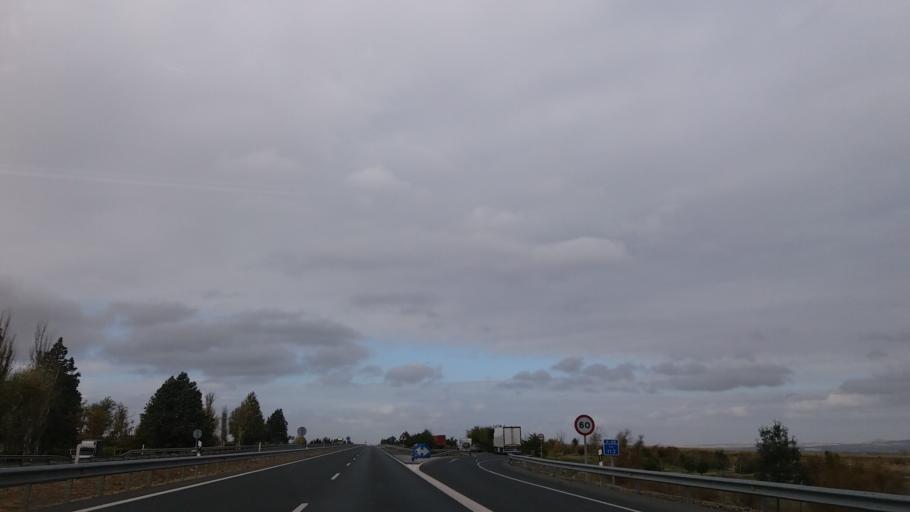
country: ES
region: Navarre
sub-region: Provincia de Navarra
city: Bunuel
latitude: 41.9391
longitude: -1.4682
